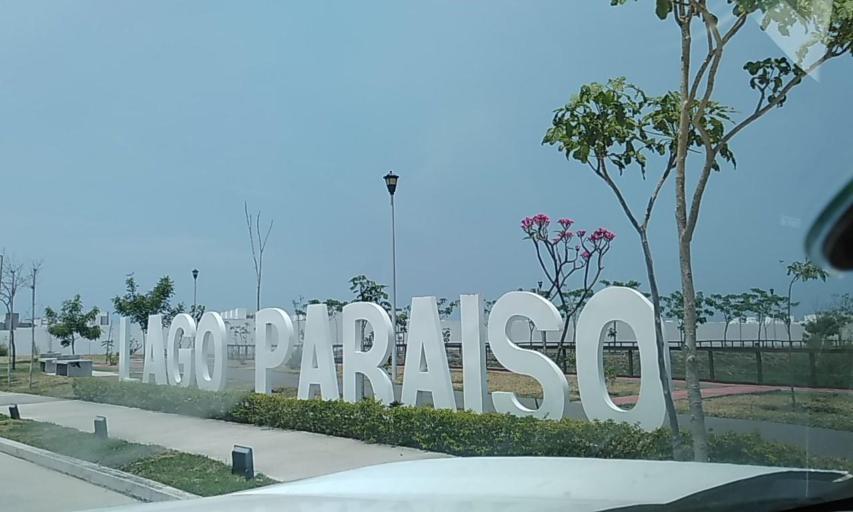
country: MX
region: Veracruz
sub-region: Veracruz
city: Hacienda Sotavento
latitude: 19.1252
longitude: -96.1712
